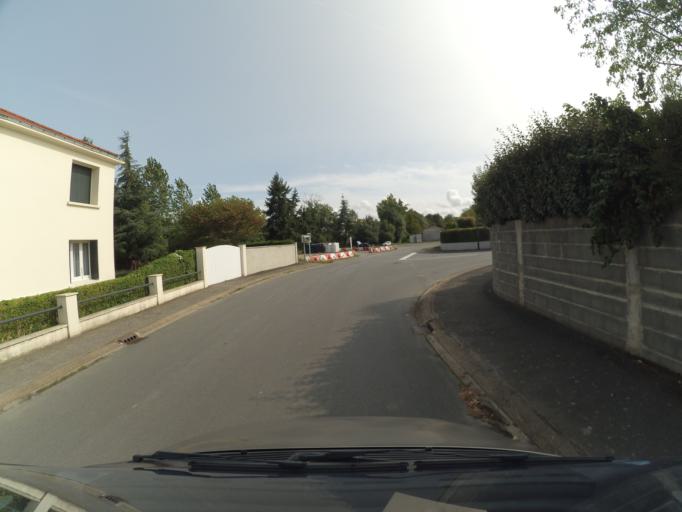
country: FR
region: Pays de la Loire
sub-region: Departement de la Vendee
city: La Bruffiere
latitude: 47.0115
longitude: -1.1967
